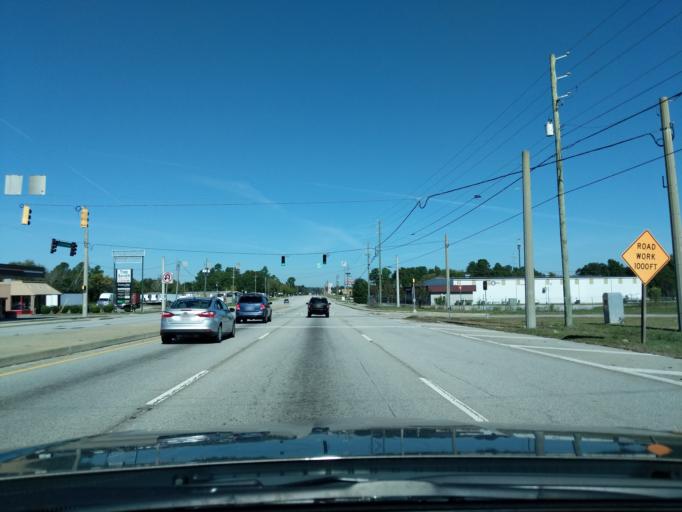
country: US
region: Georgia
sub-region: Richmond County
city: Augusta
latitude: 33.4027
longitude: -82.0059
